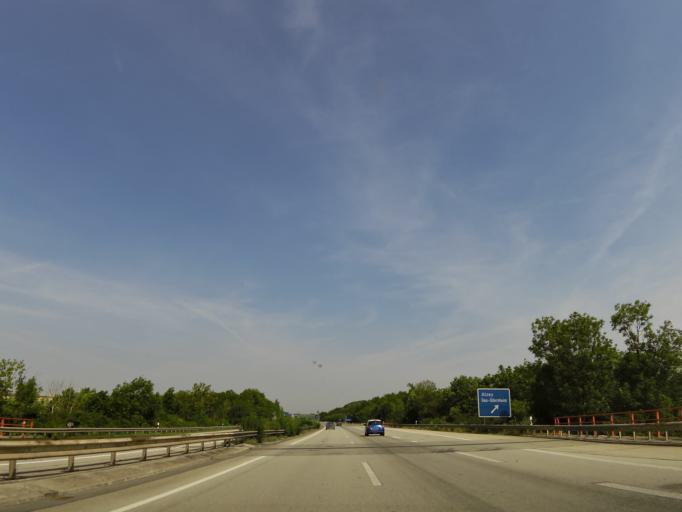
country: DE
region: Rheinland-Pfalz
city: Alzey
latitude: 49.7498
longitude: 8.1310
